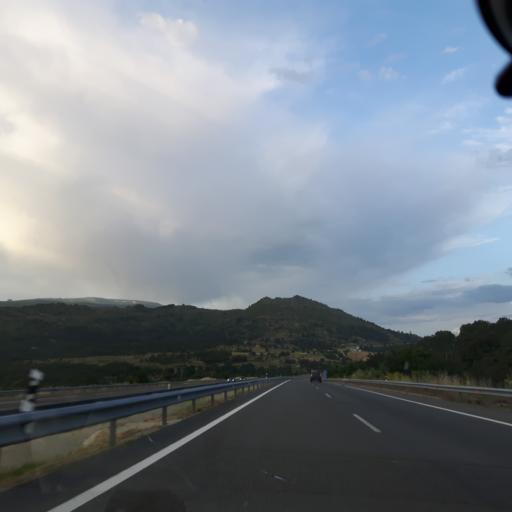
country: ES
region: Castille and Leon
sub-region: Provincia de Salamanca
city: Sorihuela
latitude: 40.4459
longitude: -5.6858
